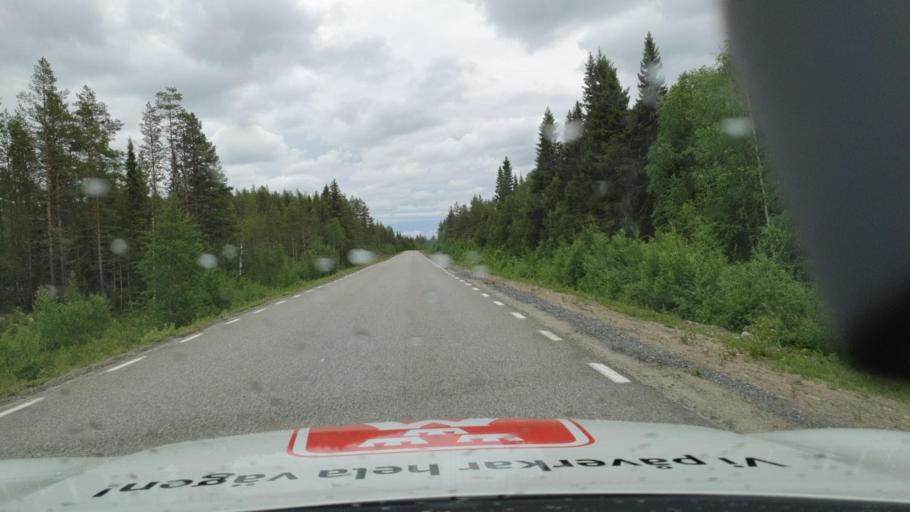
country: SE
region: Vaesterbotten
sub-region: Lycksele Kommun
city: Lycksele
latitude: 64.2433
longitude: 18.2218
